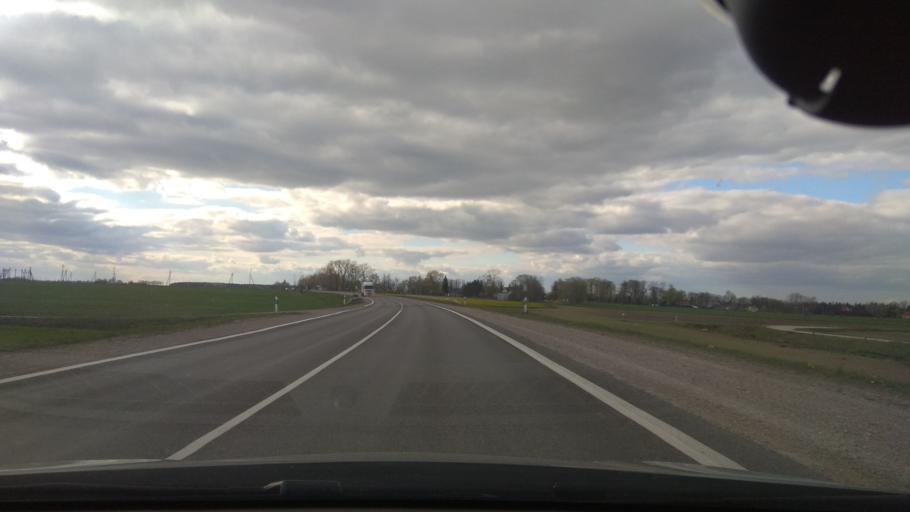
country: LT
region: Siauliu apskritis
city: Pakruojis
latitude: 55.7955
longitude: 24.0233
